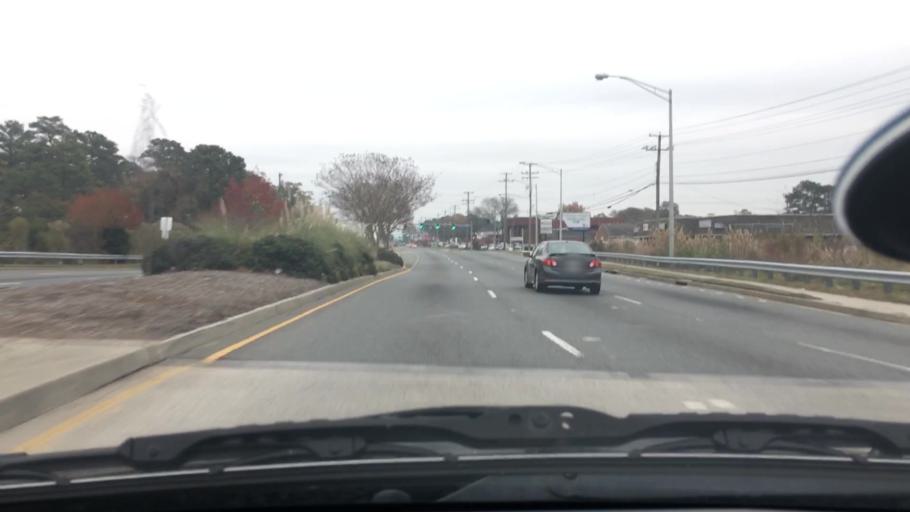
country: US
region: Virginia
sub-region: City of Norfolk
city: Norfolk
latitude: 36.8565
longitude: -76.2279
